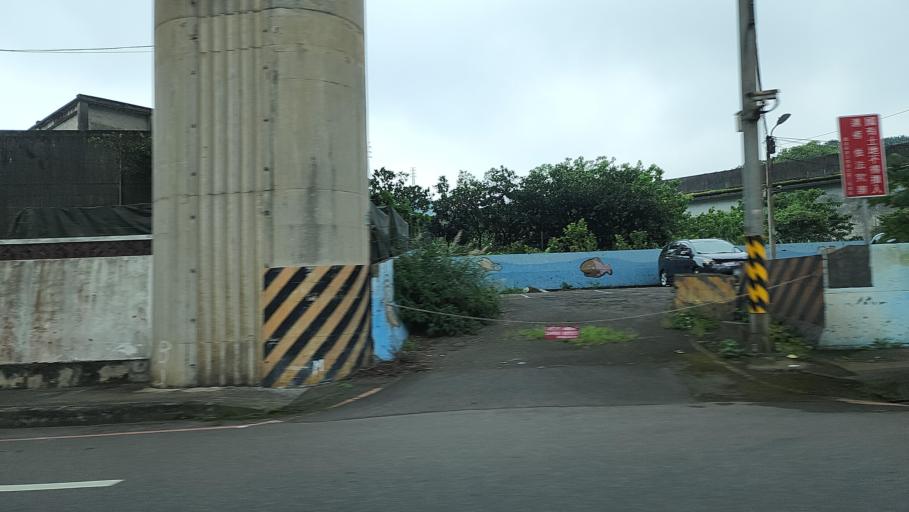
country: TW
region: Taiwan
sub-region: Keelung
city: Keelung
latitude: 25.1532
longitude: 121.7353
